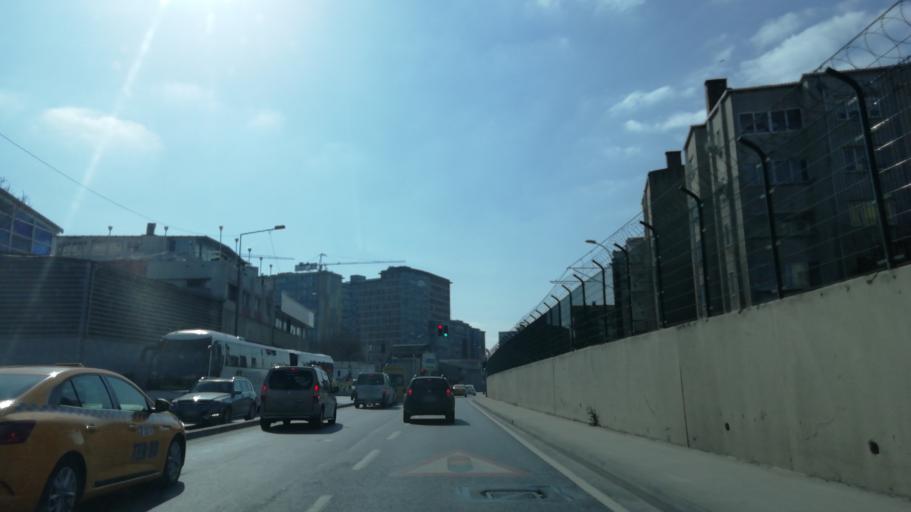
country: TR
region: Istanbul
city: guengoeren merter
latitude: 41.0143
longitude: 28.9001
